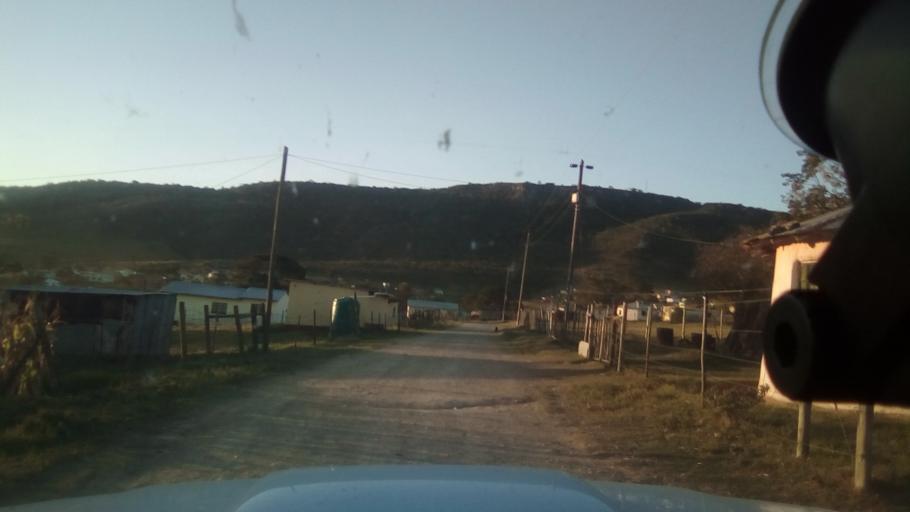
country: ZA
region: Eastern Cape
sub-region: Buffalo City Metropolitan Municipality
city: Bhisho
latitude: -32.7388
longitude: 27.3755
